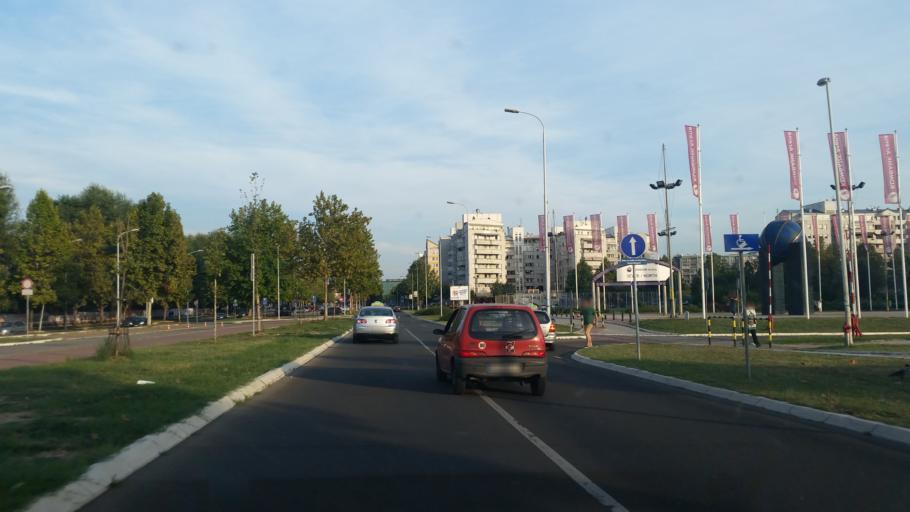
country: RS
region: Central Serbia
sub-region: Belgrade
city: Novi Beograd
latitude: 44.8158
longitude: 20.4218
